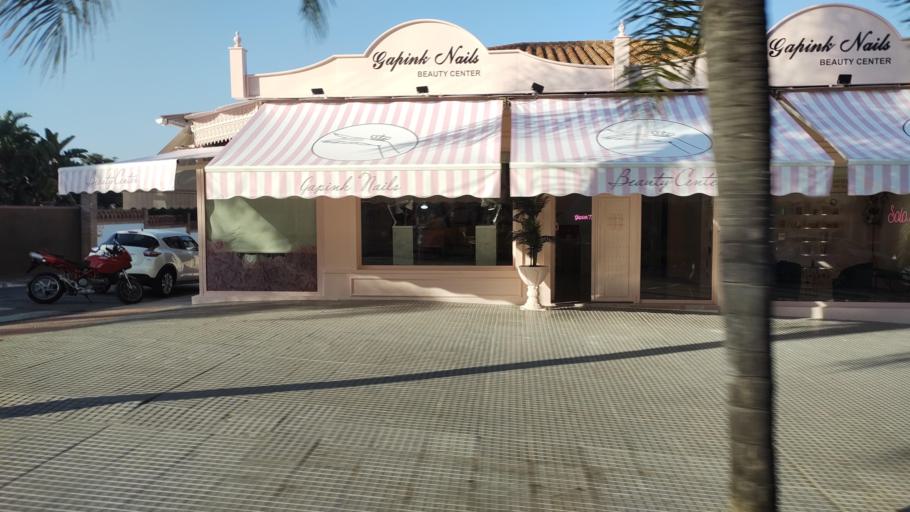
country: ES
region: Andalusia
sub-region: Provincia de Malaga
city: Torremolinos
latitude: 36.6321
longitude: -4.4943
